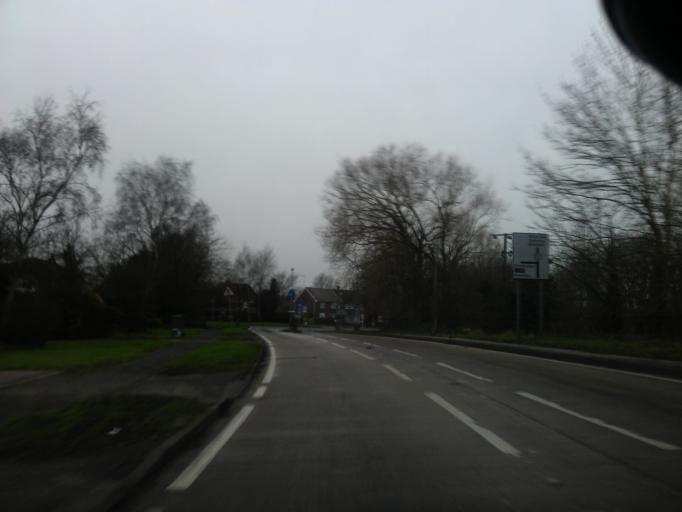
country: GB
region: England
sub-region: Essex
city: Witham
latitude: 51.8190
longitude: 0.6658
